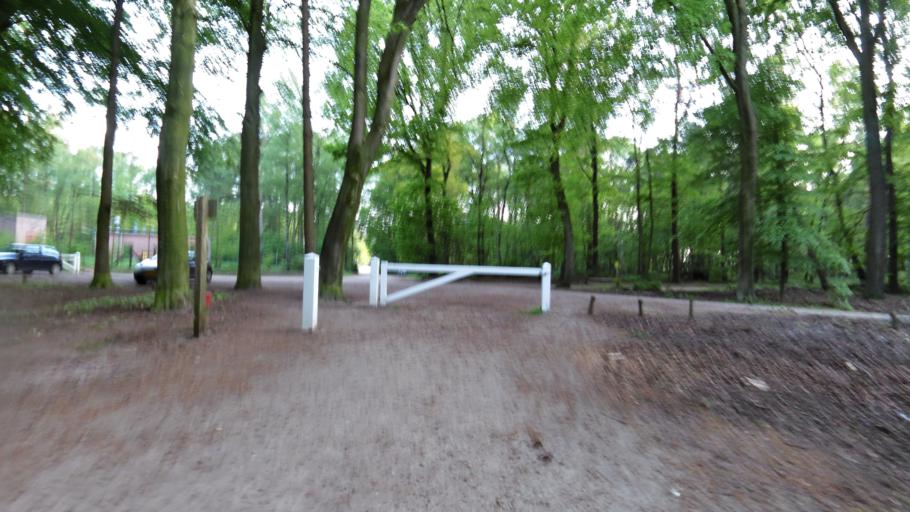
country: NL
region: Gelderland
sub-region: Gemeente Ede
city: Ede
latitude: 52.0263
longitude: 5.6868
